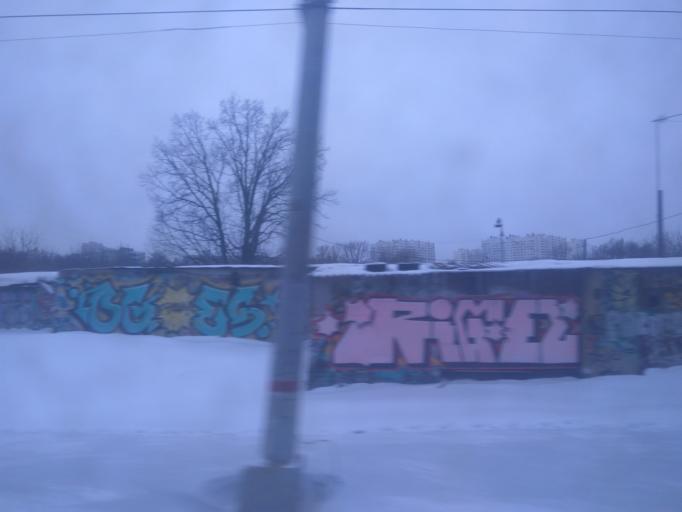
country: RU
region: Moscow
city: Tekstil'shchiki
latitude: 55.6937
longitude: 37.7316
